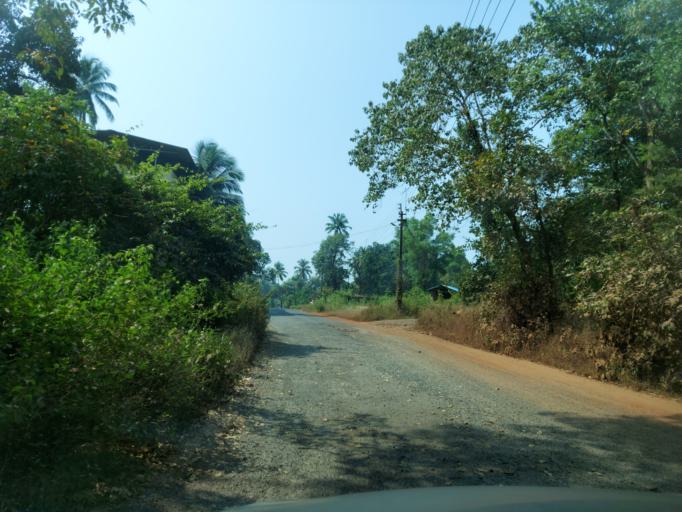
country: IN
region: Maharashtra
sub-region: Sindhudurg
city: Kudal
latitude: 15.9725
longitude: 73.6079
